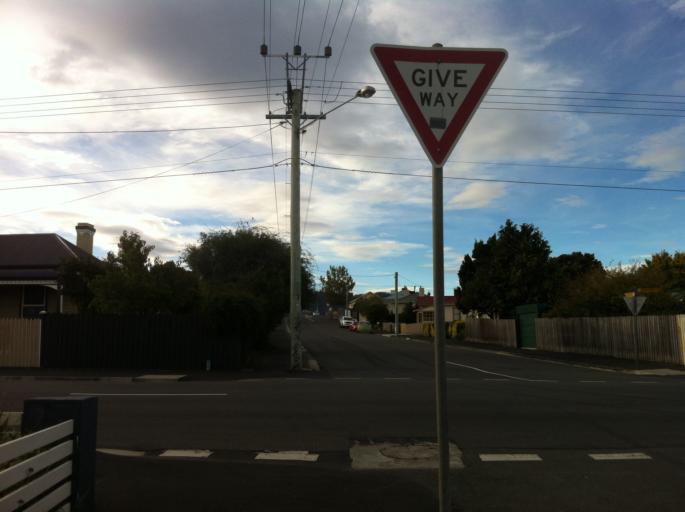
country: AU
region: Tasmania
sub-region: Glenorchy
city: Moonah
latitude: -42.8458
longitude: 147.3044
